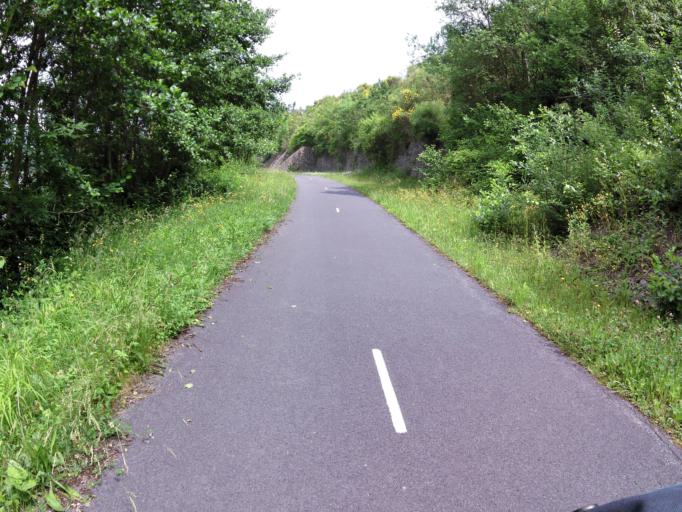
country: FR
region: Champagne-Ardenne
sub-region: Departement des Ardennes
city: Vireux-Wallerand
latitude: 50.0995
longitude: 4.7664
